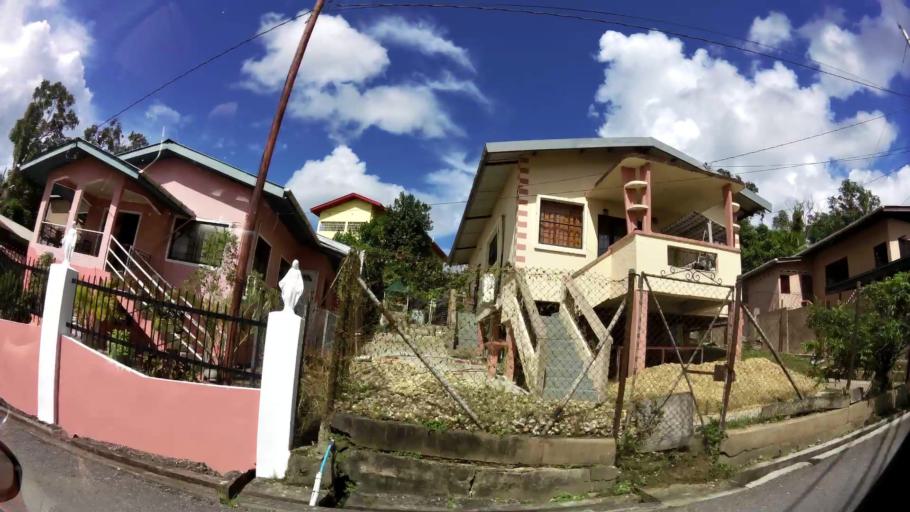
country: TT
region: Penal/Debe
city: Debe
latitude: 10.2354
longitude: -61.4396
